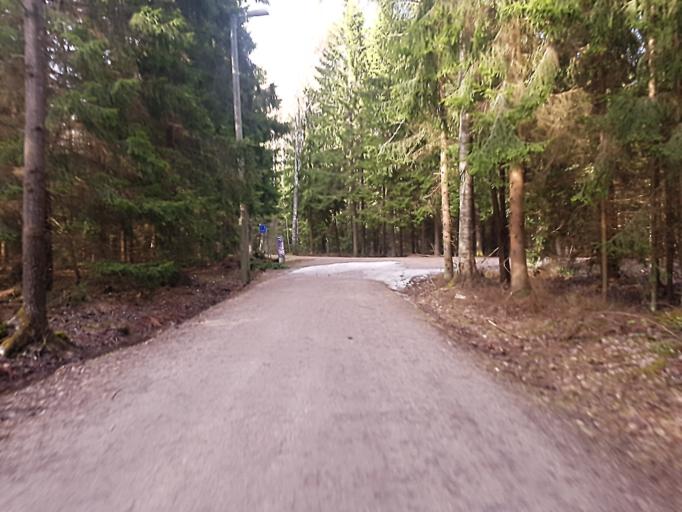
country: FI
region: Uusimaa
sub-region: Helsinki
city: Helsinki
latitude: 60.2573
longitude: 24.9278
